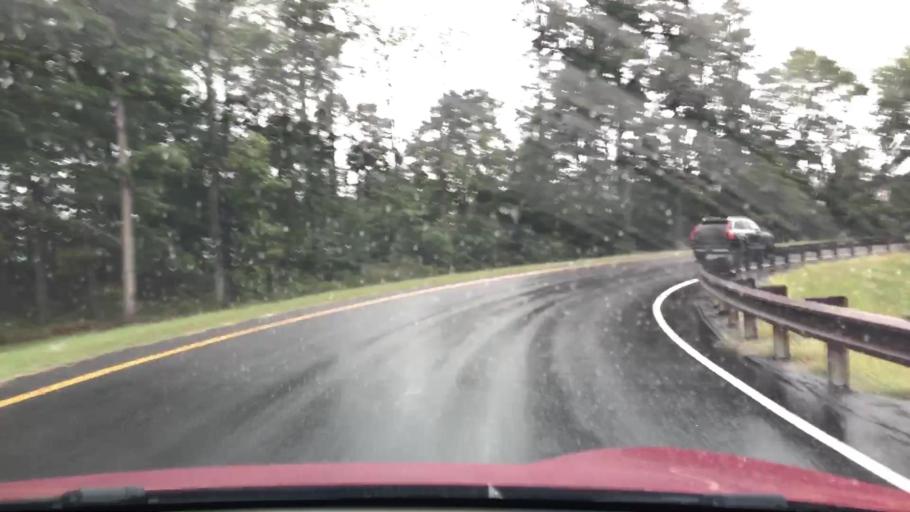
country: US
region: New Jersey
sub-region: Atlantic County
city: Northfield
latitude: 39.3975
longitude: -74.5631
